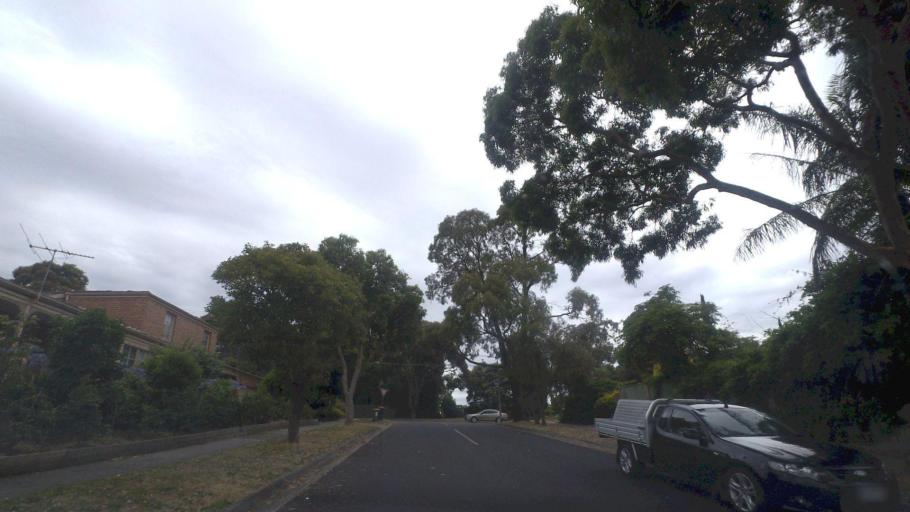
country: AU
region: Victoria
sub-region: Knox
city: Wantirna
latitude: -37.8563
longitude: 145.2261
